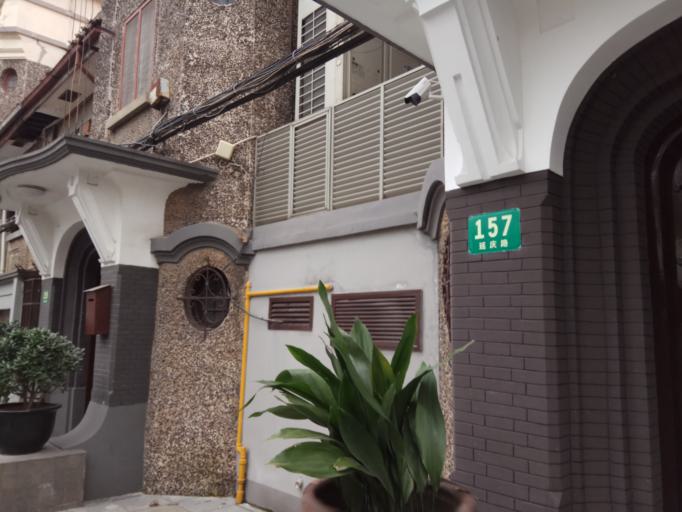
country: CN
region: Shanghai Shi
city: Shanghai
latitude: 31.2165
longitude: 121.4450
